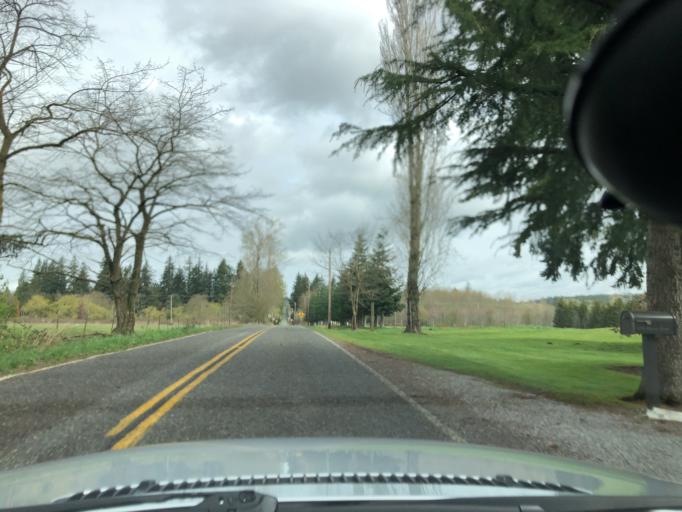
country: US
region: Washington
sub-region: Whatcom County
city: Blaine
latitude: 48.9768
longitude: -122.7039
